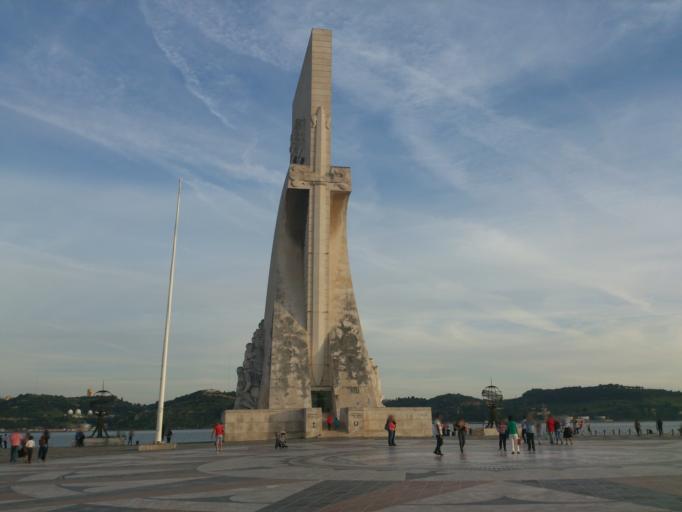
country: PT
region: Lisbon
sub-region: Oeiras
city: Alges
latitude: 38.6944
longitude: -9.2058
